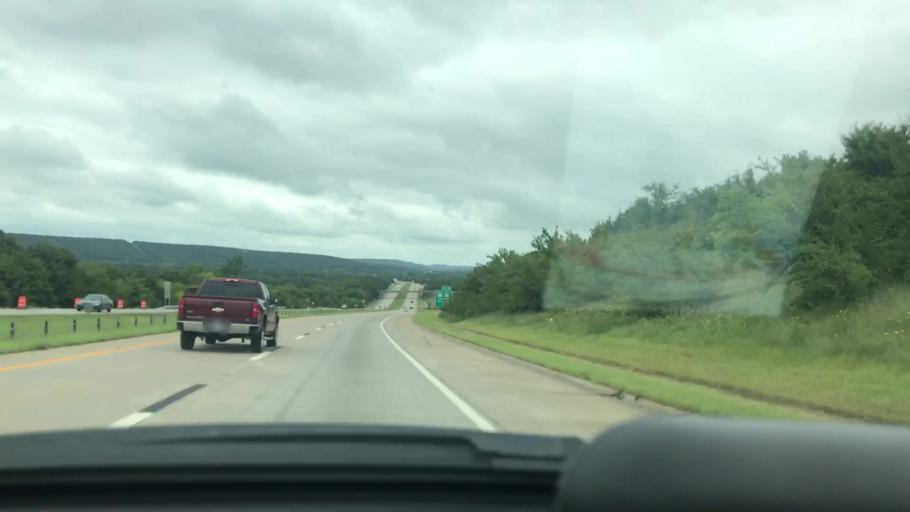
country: US
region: Oklahoma
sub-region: Pittsburg County
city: Krebs
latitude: 34.9927
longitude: -95.7214
